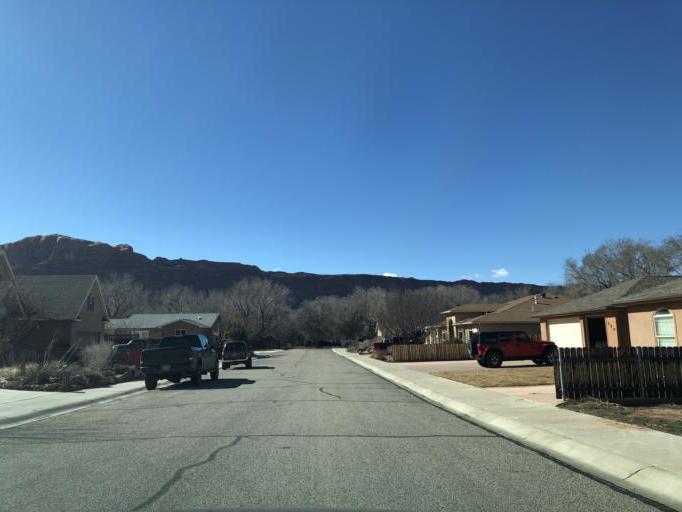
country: US
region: Utah
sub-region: Grand County
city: Moab
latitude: 38.5826
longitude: -109.5621
